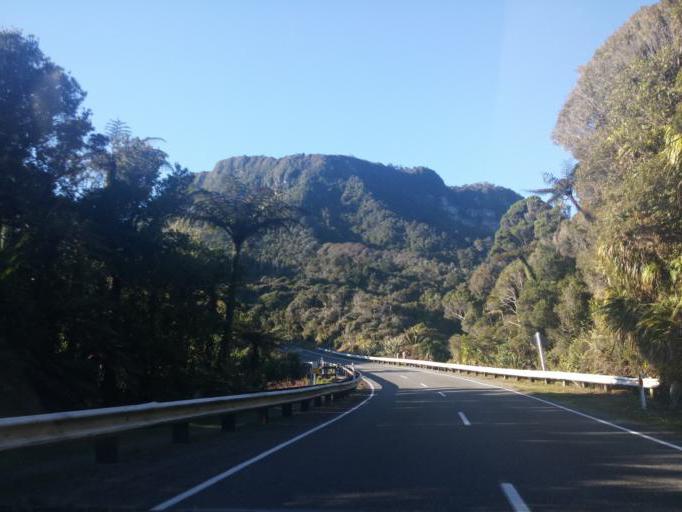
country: NZ
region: West Coast
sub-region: Grey District
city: Greymouth
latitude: -42.1011
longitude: 171.3408
